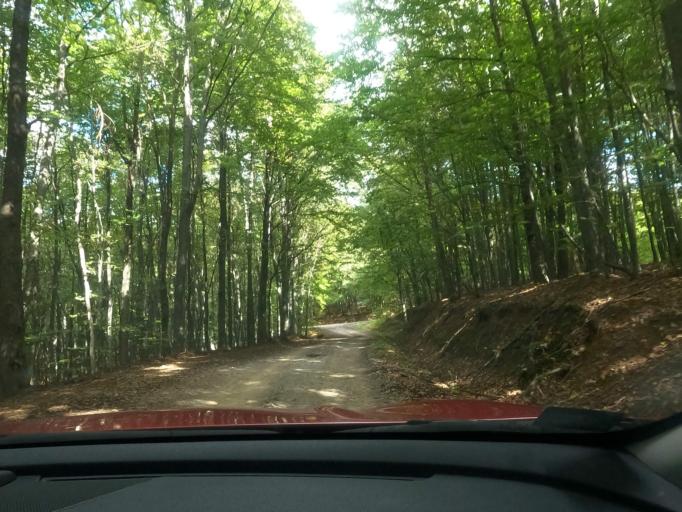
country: BA
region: Federation of Bosnia and Herzegovina
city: Velika Kladusa
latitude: 45.2645
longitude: 15.7794
